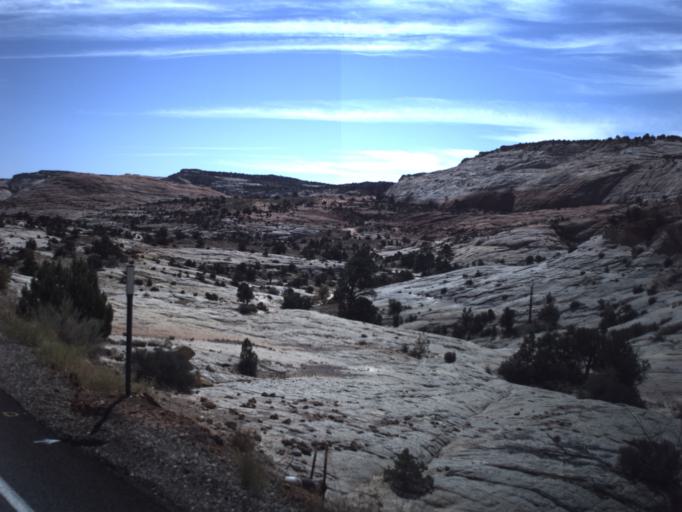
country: US
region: Utah
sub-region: Wayne County
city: Loa
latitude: 37.7502
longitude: -111.4449
